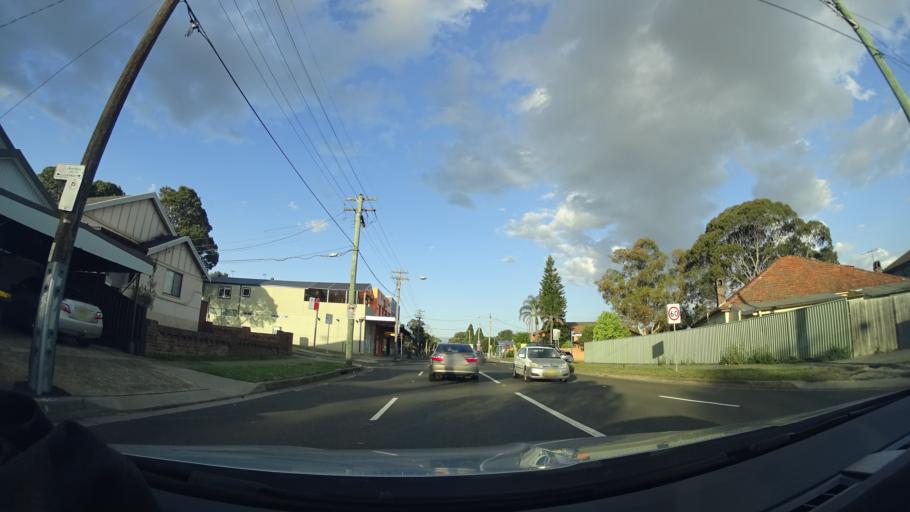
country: AU
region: New South Wales
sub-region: Canterbury
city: Belfield
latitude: -33.8970
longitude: 151.1016
